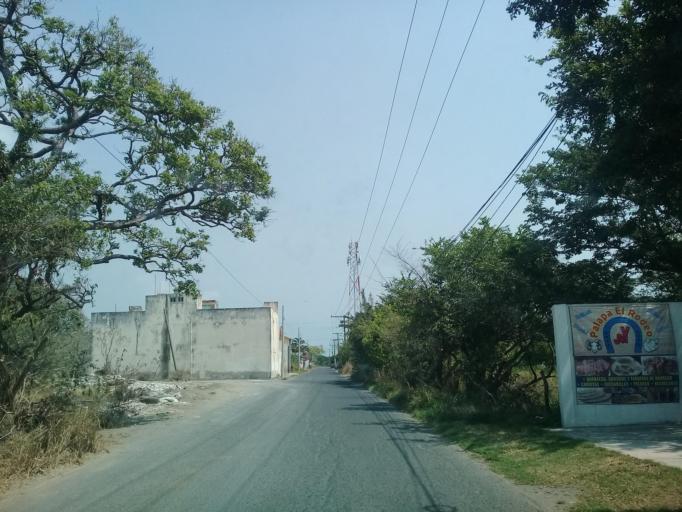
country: MX
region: Veracruz
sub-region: Veracruz
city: Hacienda Sotavento
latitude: 19.1337
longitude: -96.1777
